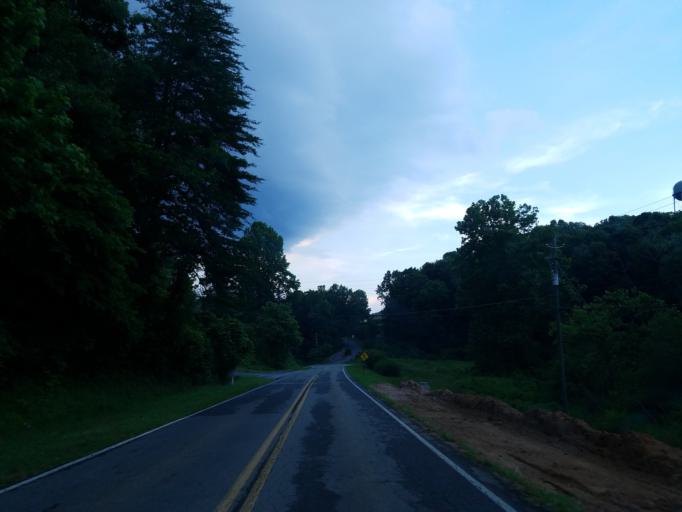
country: US
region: Georgia
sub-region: Lumpkin County
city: Dahlonega
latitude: 34.5413
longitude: -83.9816
